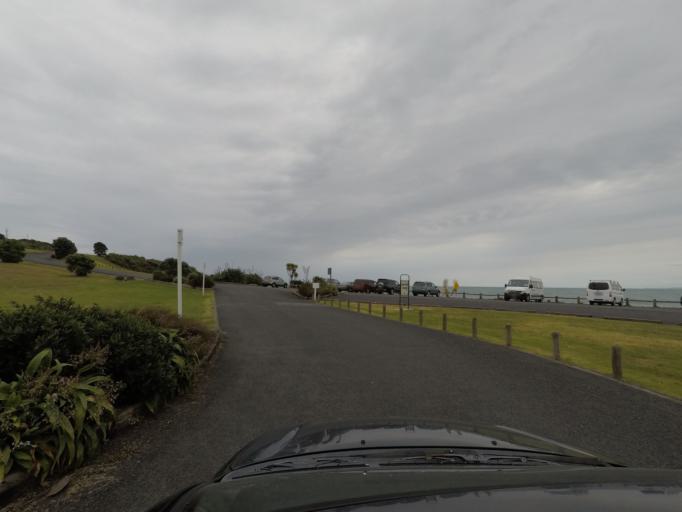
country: NZ
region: Waikato
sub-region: Waikato District
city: Raglan
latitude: -37.8216
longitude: 174.8126
